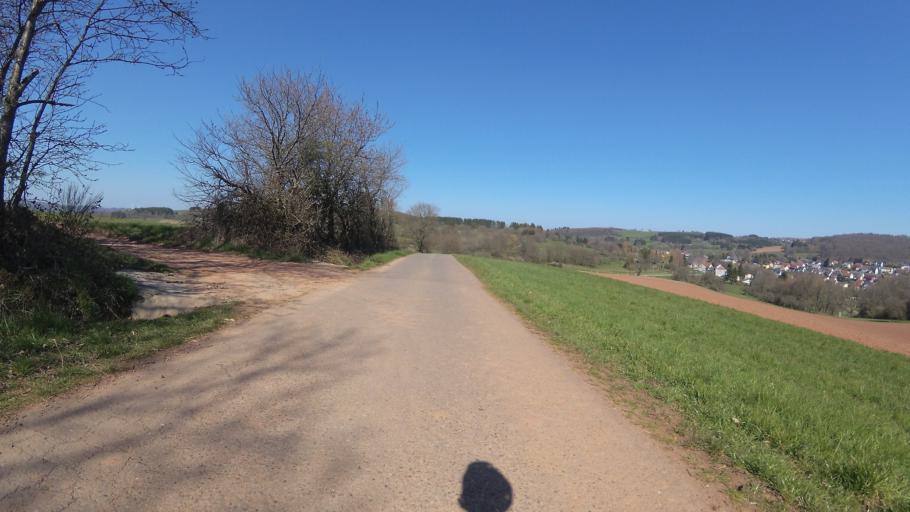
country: DE
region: Rheinland-Pfalz
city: Breitenbach
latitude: 49.4148
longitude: 7.2532
